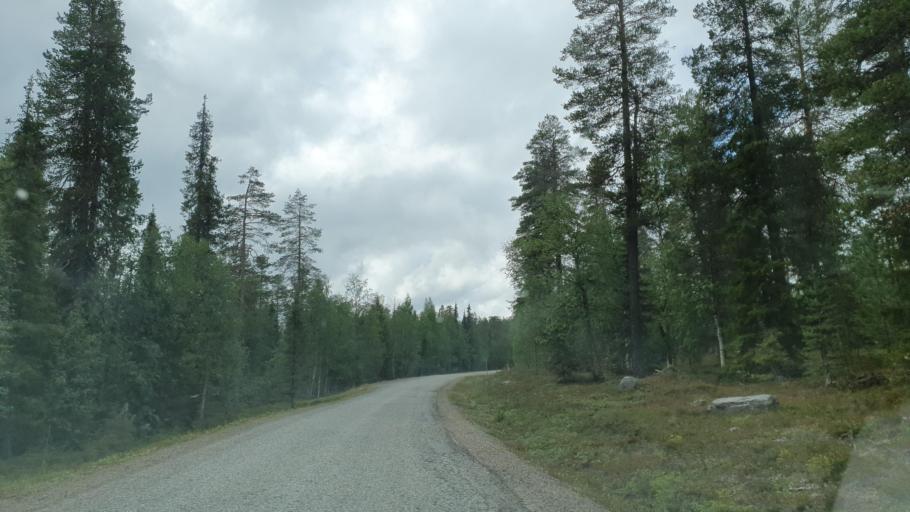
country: FI
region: Lapland
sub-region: Tunturi-Lappi
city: Muonio
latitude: 67.7048
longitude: 24.1941
